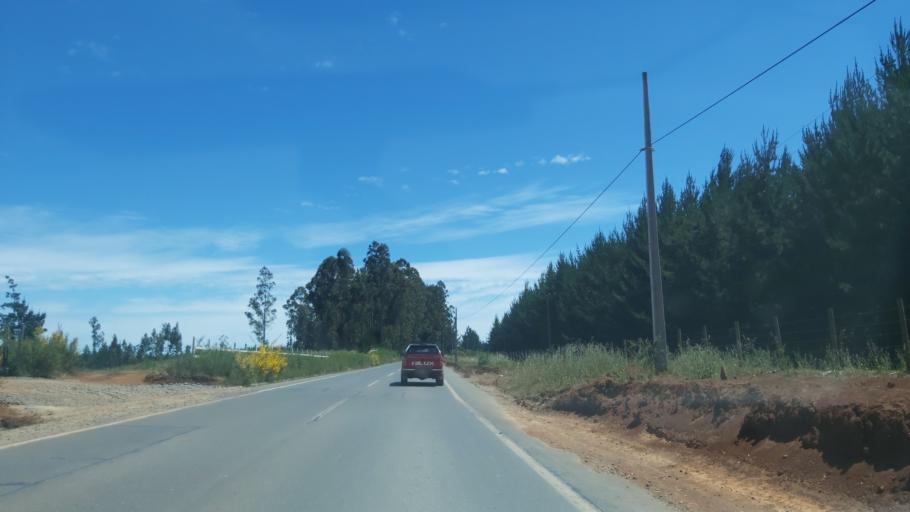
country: CL
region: Maule
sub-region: Provincia de Talca
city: Constitucion
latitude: -35.3952
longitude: -72.4294
